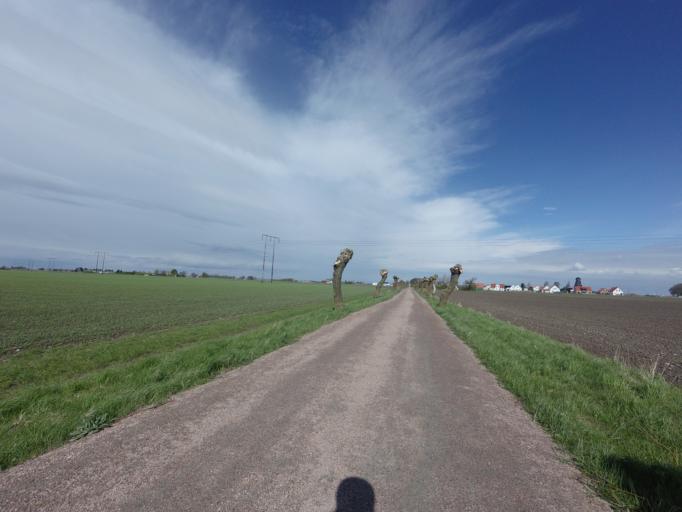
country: SE
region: Skane
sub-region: Malmo
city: Tygelsjo
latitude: 55.5228
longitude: 12.9890
